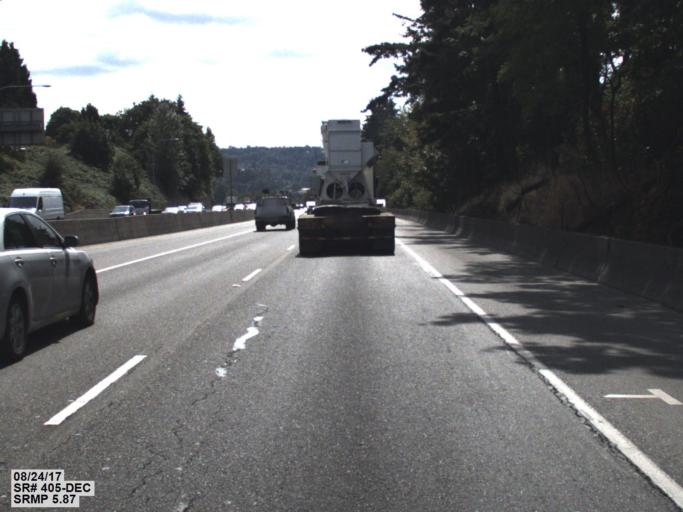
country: US
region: Washington
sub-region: King County
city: Renton
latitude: 47.5091
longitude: -122.1982
